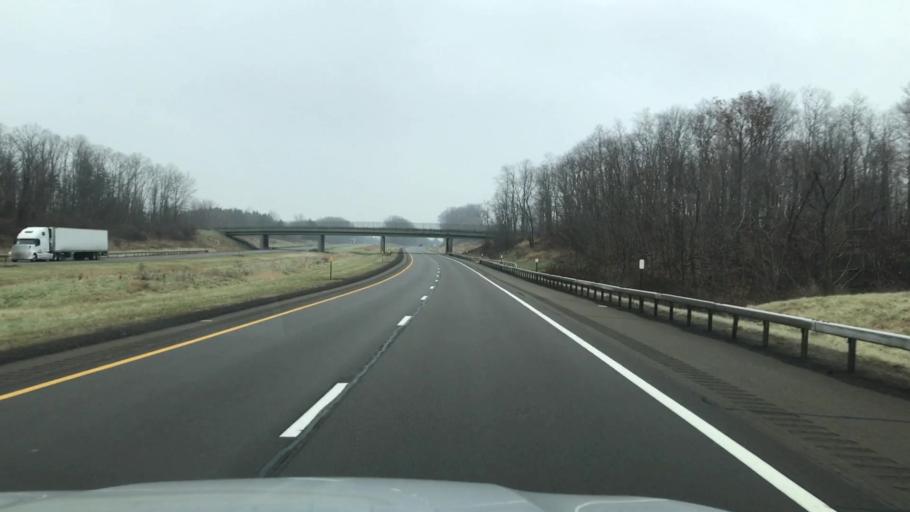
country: US
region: New York
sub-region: Chautauqua County
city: Brocton
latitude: 42.4202
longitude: -79.4014
